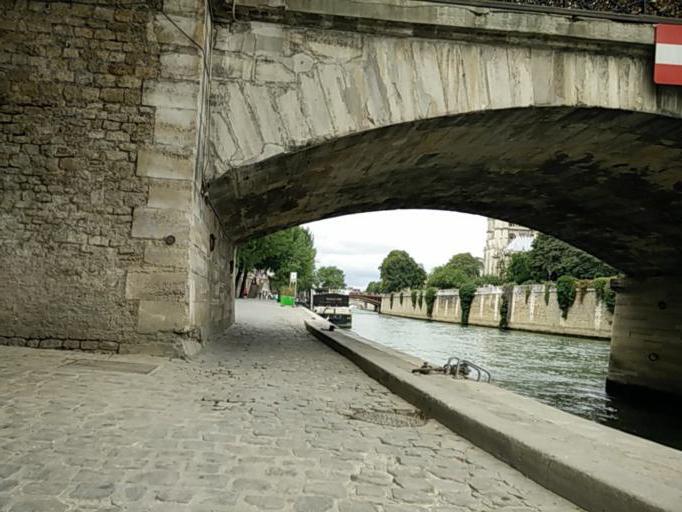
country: FR
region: Ile-de-France
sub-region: Paris
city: Paris
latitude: 48.8513
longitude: 2.3517
